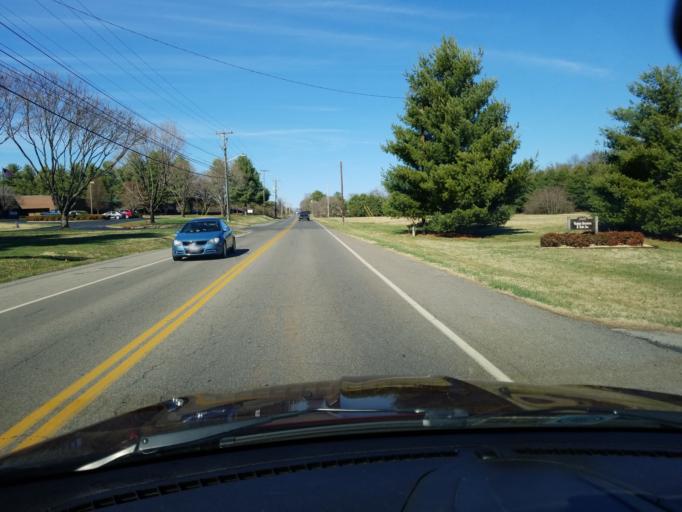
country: US
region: Virginia
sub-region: Roanoke County
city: Hollins
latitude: 37.3411
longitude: -79.9255
